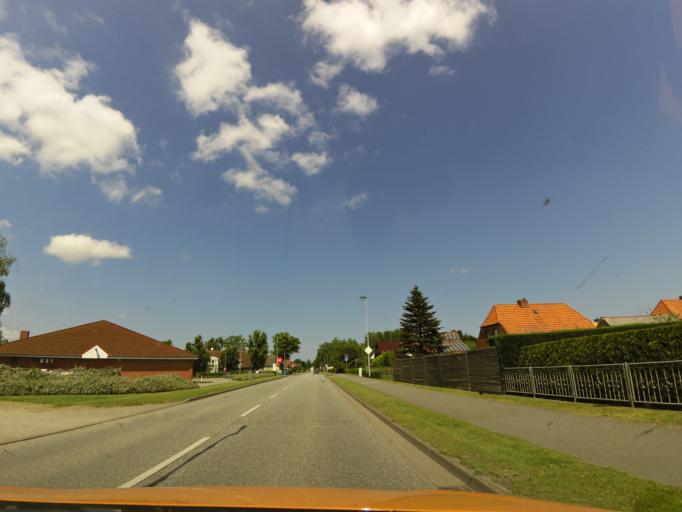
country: DE
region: Mecklenburg-Vorpommern
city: Rehna
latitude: 53.7736
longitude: 11.0517
